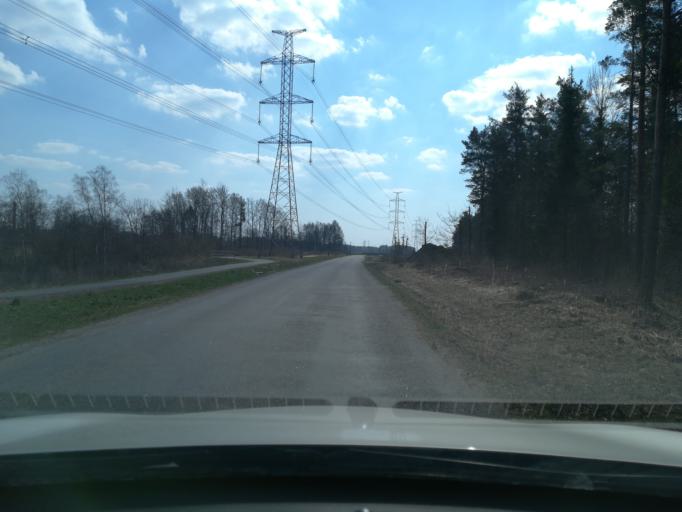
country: EE
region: Harju
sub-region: Saue vald
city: Laagri
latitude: 59.3533
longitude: 24.5888
